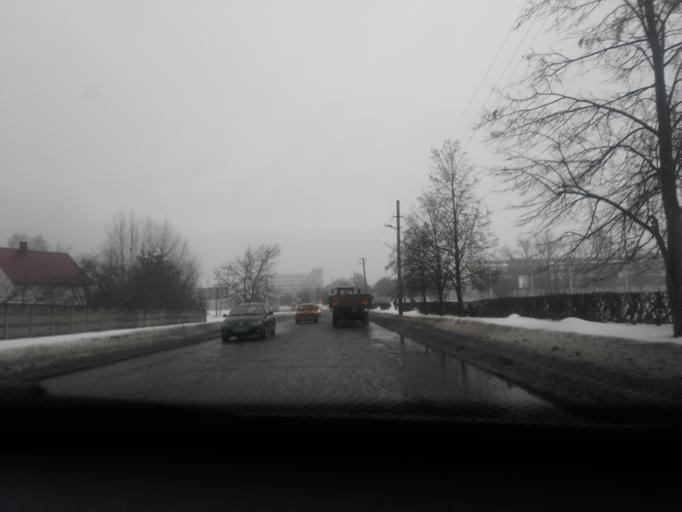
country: BY
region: Mogilev
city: Babruysk
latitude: 53.1852
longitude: 29.2140
